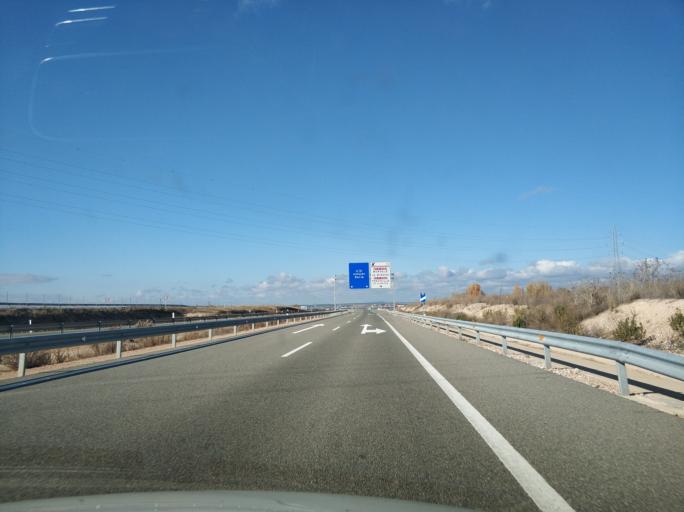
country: ES
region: Castille and Leon
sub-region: Provincia de Soria
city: Frechilla de Almazan
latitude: 41.4416
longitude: -2.5026
